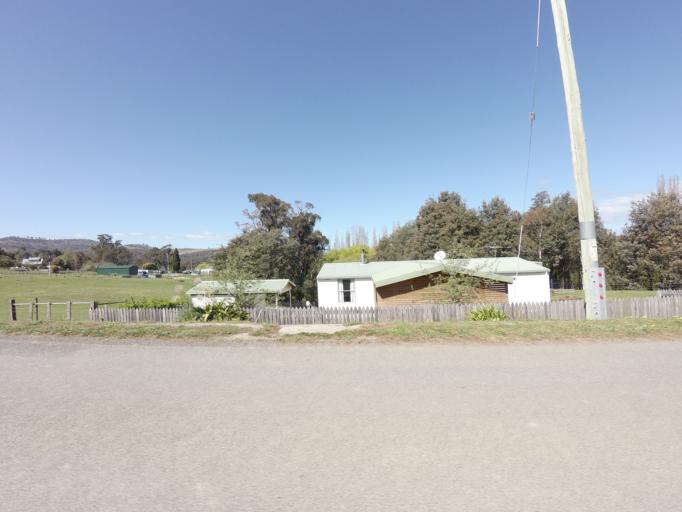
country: AU
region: Tasmania
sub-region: Derwent Valley
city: New Norfolk
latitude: -42.6707
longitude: 146.7901
